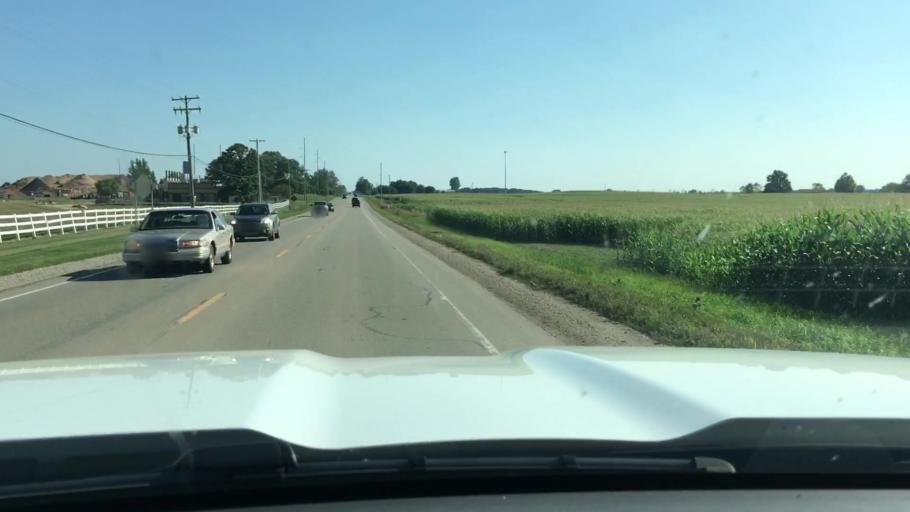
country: US
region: Michigan
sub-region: Ottawa County
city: Coopersville
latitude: 43.0502
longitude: -85.9568
